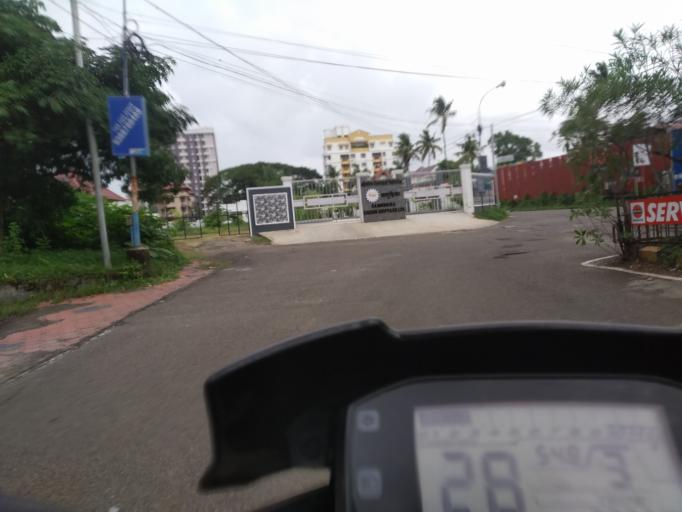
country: IN
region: Kerala
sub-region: Ernakulam
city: Cochin
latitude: 9.9528
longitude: 76.2968
